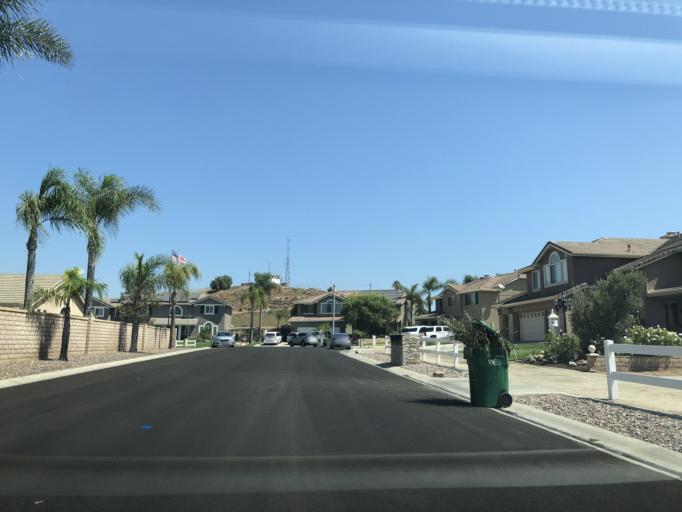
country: US
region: California
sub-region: Riverside County
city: Norco
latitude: 33.9197
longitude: -117.5744
